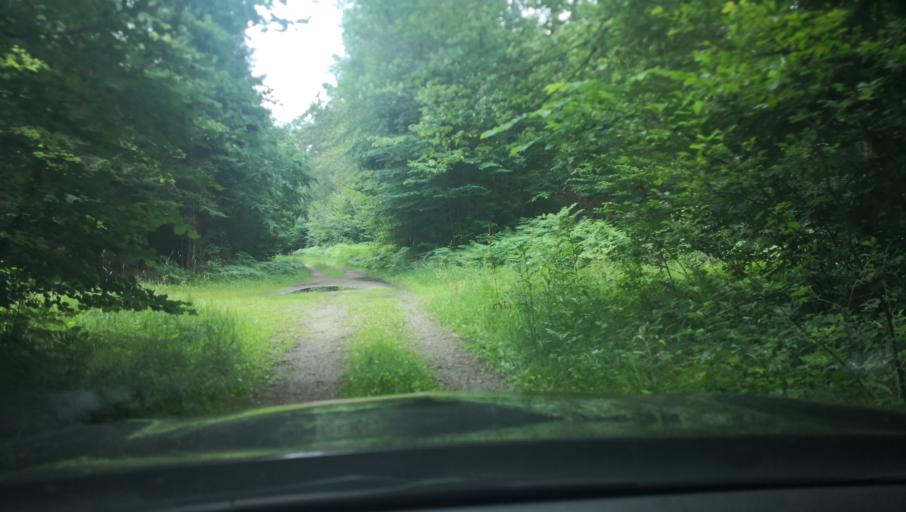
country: SE
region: Skane
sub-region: Simrishamns Kommun
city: Kivik
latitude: 55.6168
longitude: 14.1070
